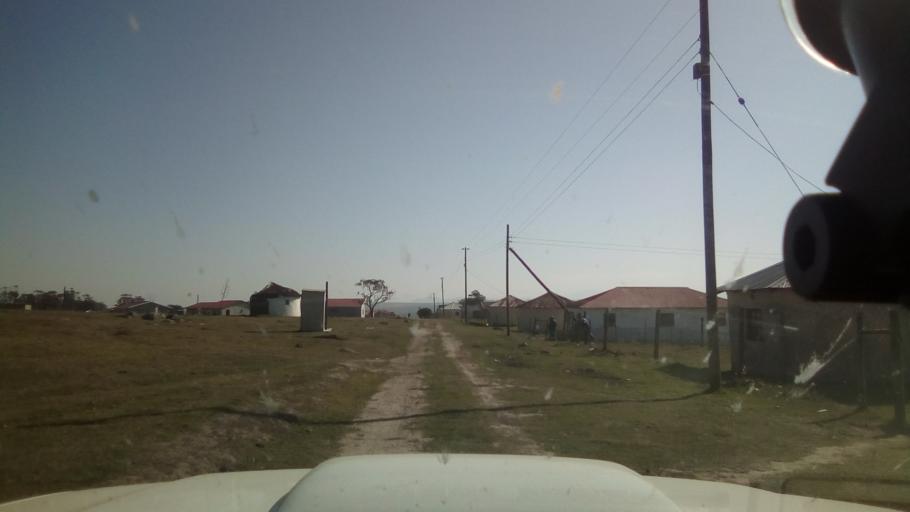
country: ZA
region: Eastern Cape
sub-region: Buffalo City Metropolitan Municipality
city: Bhisho
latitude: -32.9390
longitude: 27.3392
